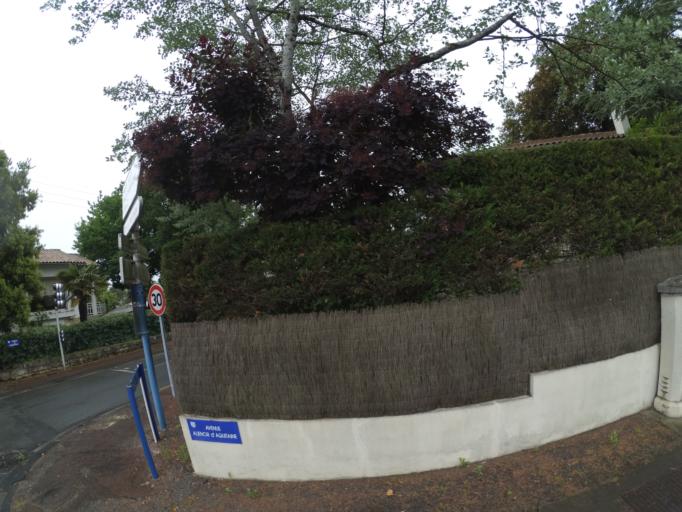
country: FR
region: Poitou-Charentes
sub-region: Departement de la Charente-Maritime
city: Saint-Georges-de-Didonne
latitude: 45.6193
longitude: -1.0070
